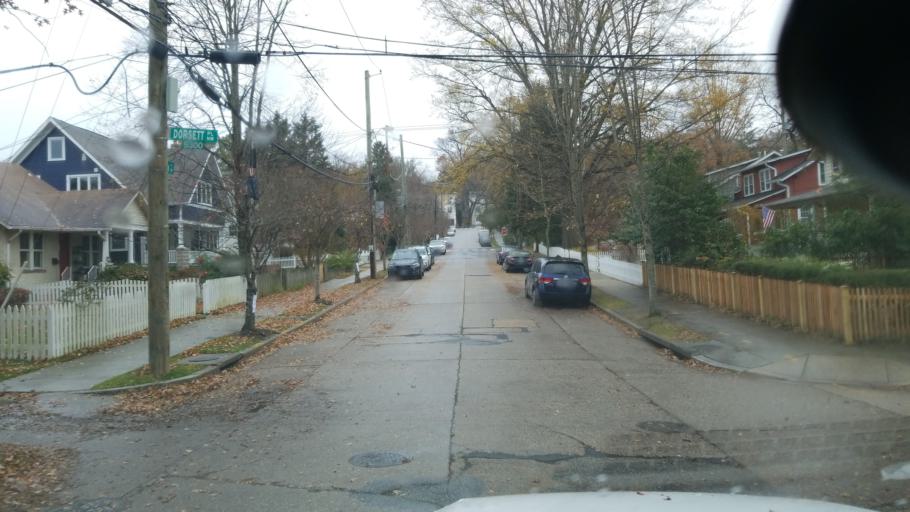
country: US
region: Maryland
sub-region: Montgomery County
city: Brookmont
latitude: 38.9277
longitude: -77.1075
